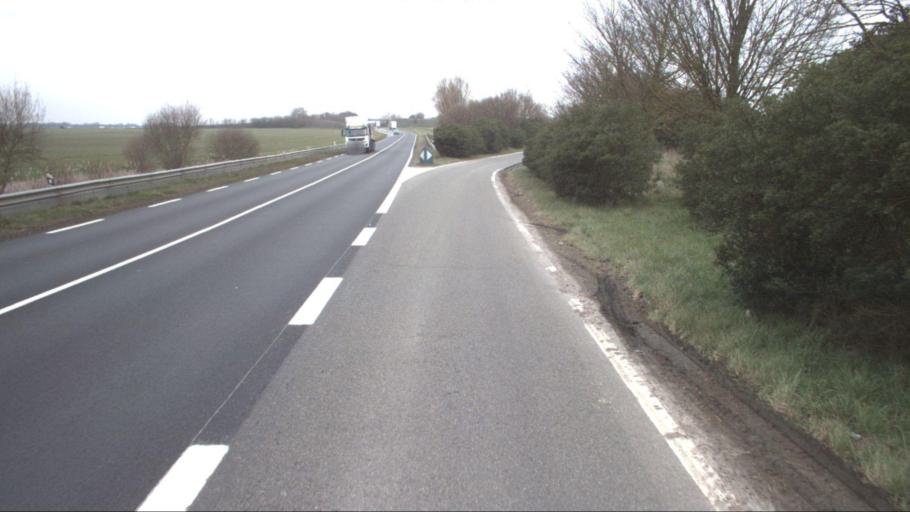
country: FR
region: Ile-de-France
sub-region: Departement des Yvelines
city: Ablis
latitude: 48.5050
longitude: 1.8369
